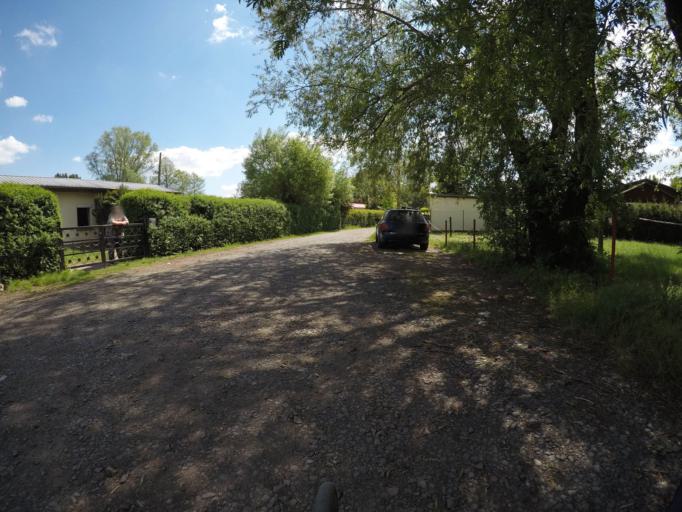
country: DE
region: Brandenburg
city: Werder
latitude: 52.3993
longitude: 12.9432
